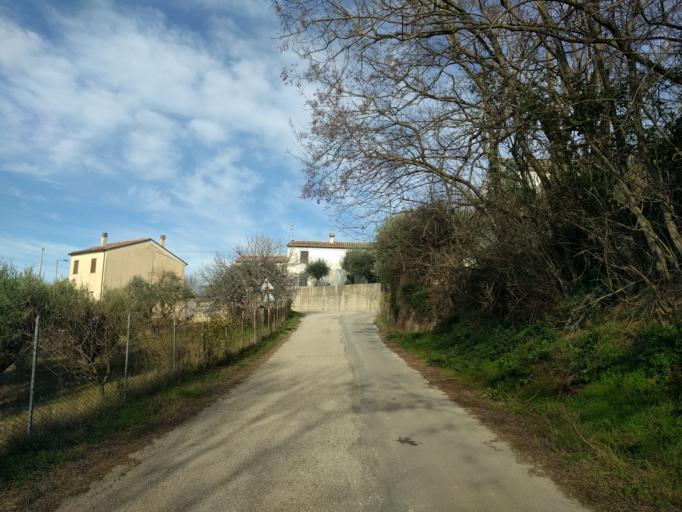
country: IT
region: The Marches
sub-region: Provincia di Pesaro e Urbino
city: Cuccurano
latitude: 43.8096
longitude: 12.9516
